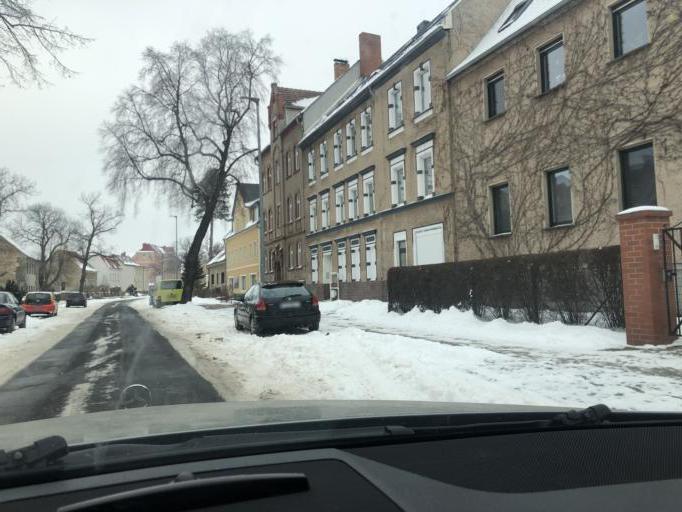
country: DE
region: Brandenburg
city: Guben
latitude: 51.9455
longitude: 14.7088
